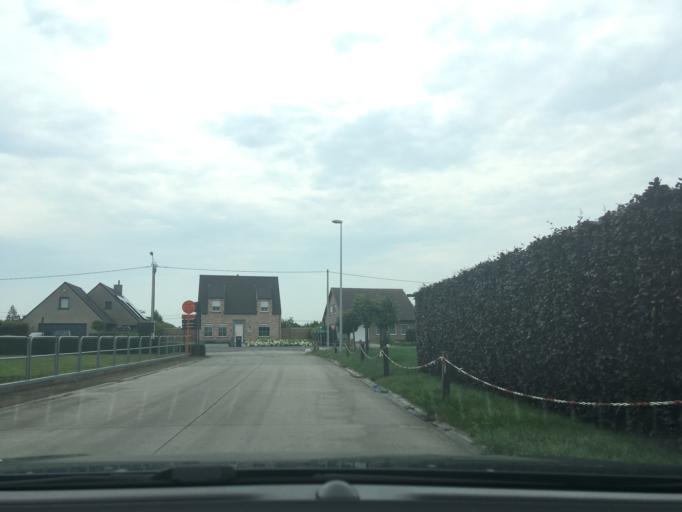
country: BE
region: Flanders
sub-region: Provincie West-Vlaanderen
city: Lichtervelde
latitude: 51.0246
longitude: 3.1173
